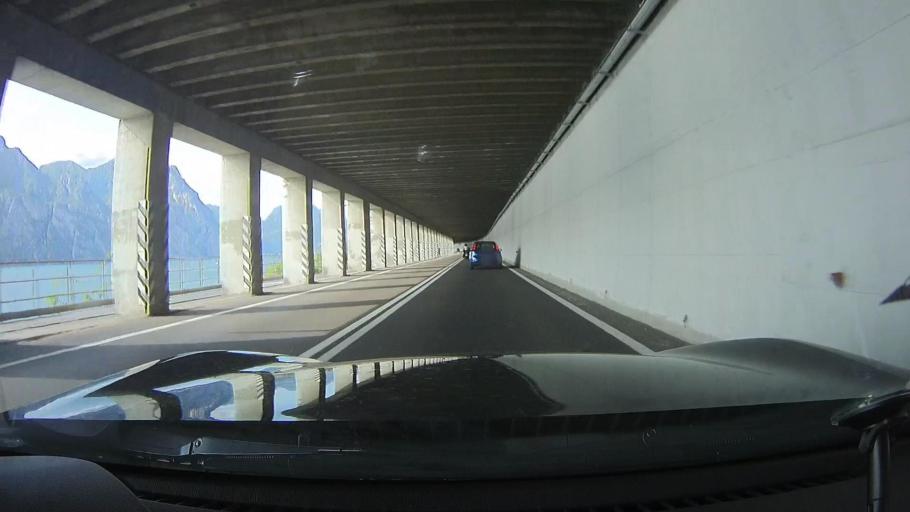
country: IT
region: Trentino-Alto Adige
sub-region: Provincia di Trento
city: Torbole sul Garda
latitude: 45.8216
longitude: 10.8555
